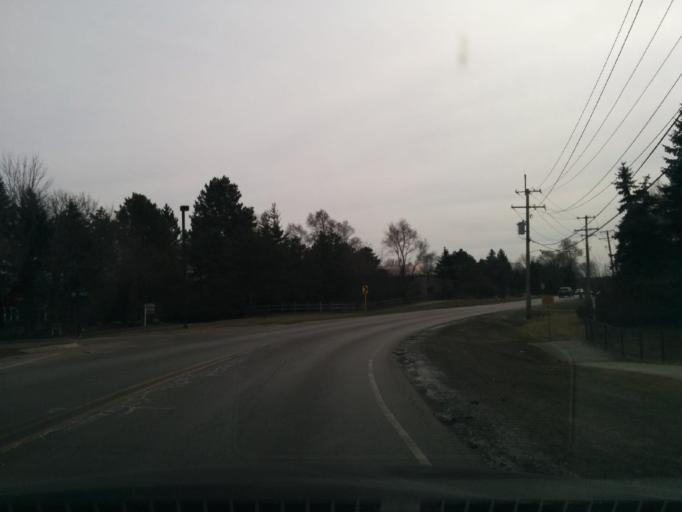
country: US
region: Illinois
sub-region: DuPage County
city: Oak Brook
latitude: 41.8246
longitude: -87.9258
